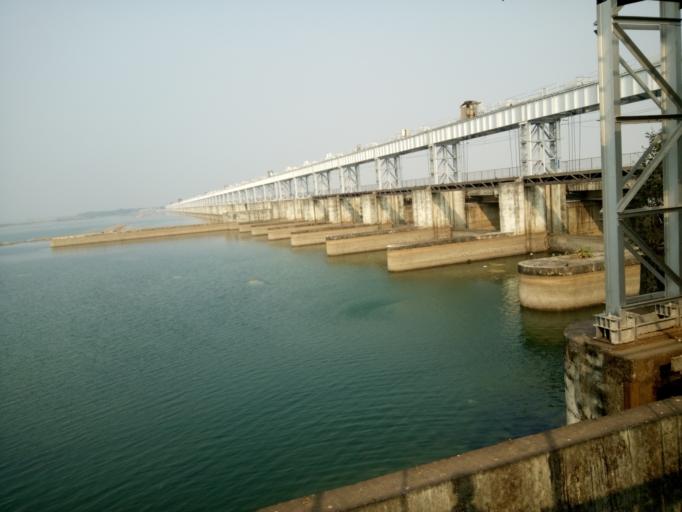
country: IN
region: Odisha
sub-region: Cuttack
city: Cuttack
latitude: 20.4773
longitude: 85.8983
